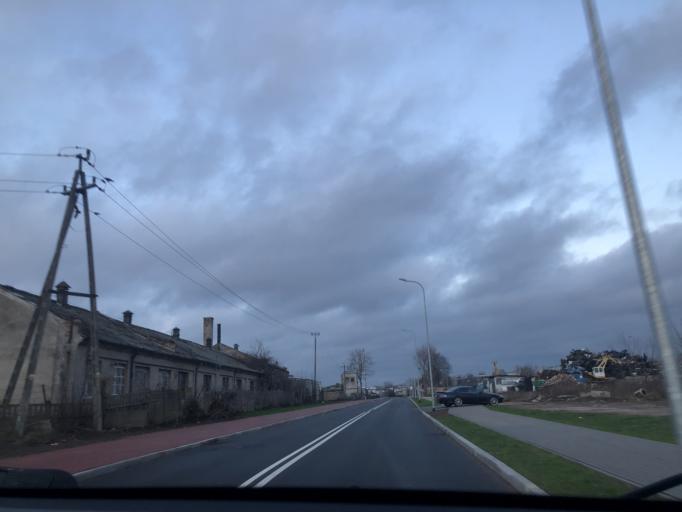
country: PL
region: Podlasie
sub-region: Lomza
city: Lomza
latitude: 53.1713
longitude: 22.0614
